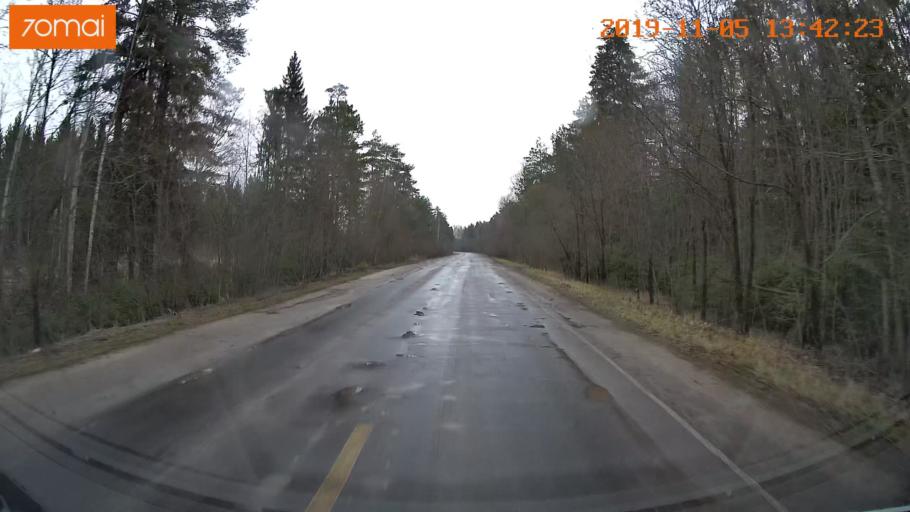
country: RU
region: Ivanovo
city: Shuya
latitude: 56.9662
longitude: 41.3934
